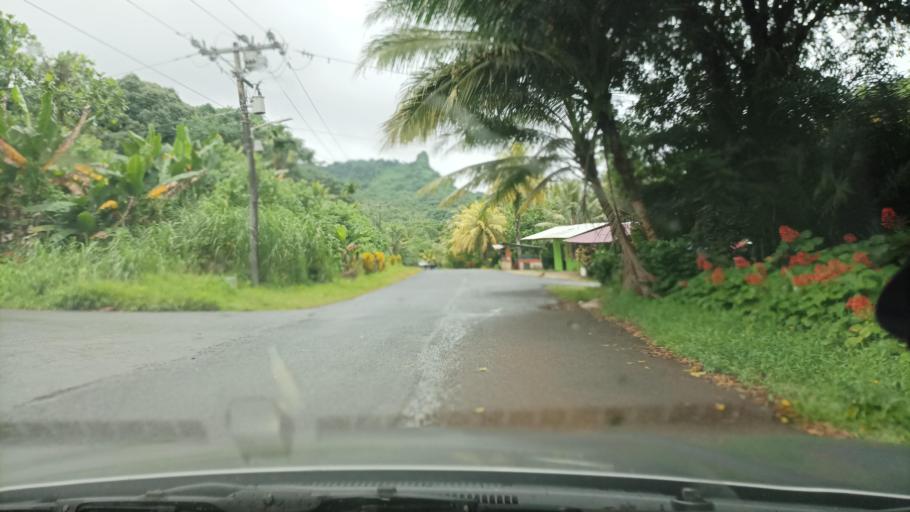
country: FM
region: Pohnpei
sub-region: Madolenihm Municipality
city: Madolenihm Municipality Government
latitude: 6.8130
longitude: 158.2431
